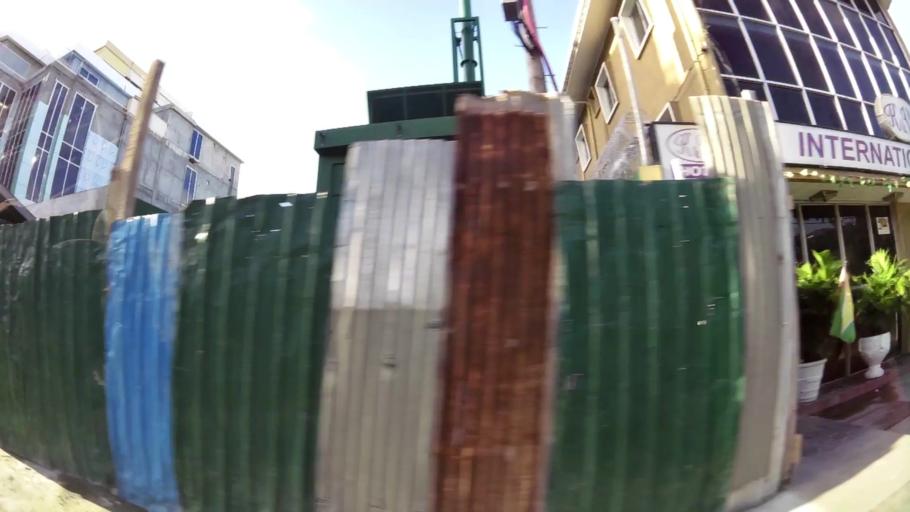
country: GY
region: Demerara-Mahaica
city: Georgetown
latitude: 6.8086
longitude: -58.1606
